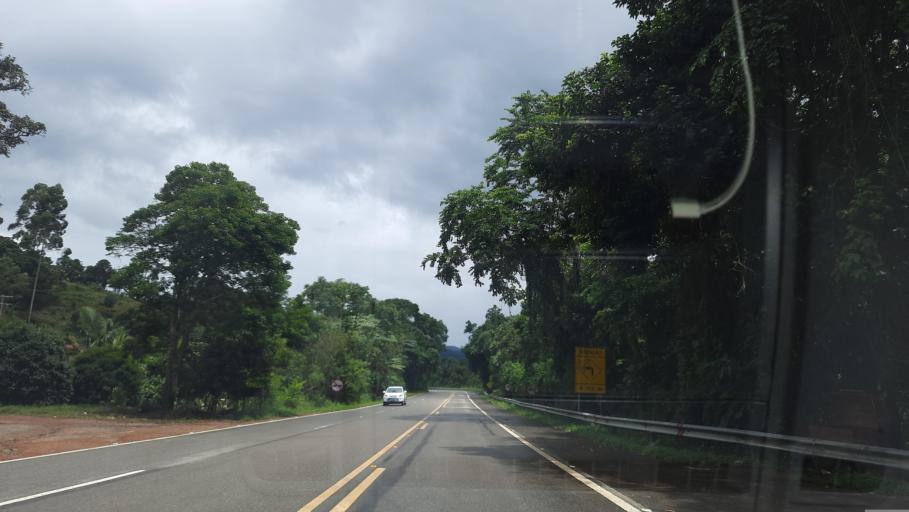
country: BR
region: Minas Gerais
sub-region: Pocos De Caldas
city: Pocos de Caldas
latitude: -21.8448
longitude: -46.6916
